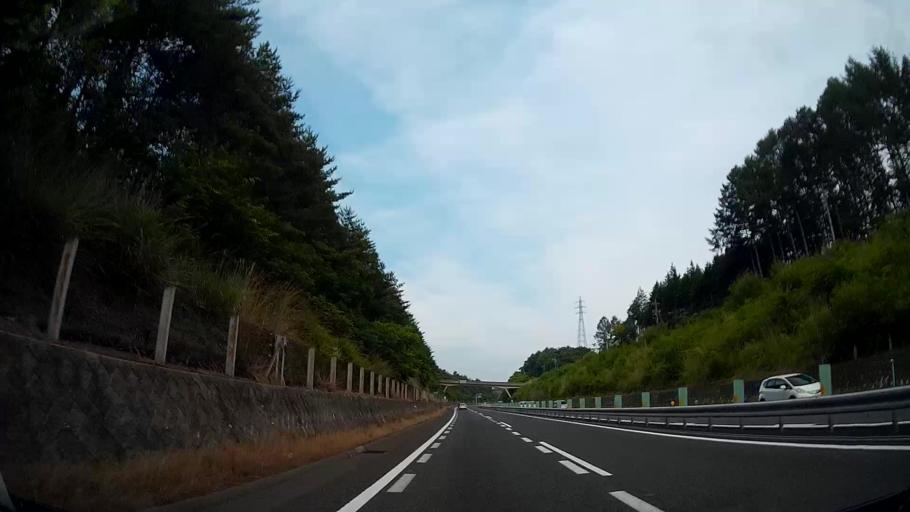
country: JP
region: Nagano
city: Chino
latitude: 35.9712
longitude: 138.1792
